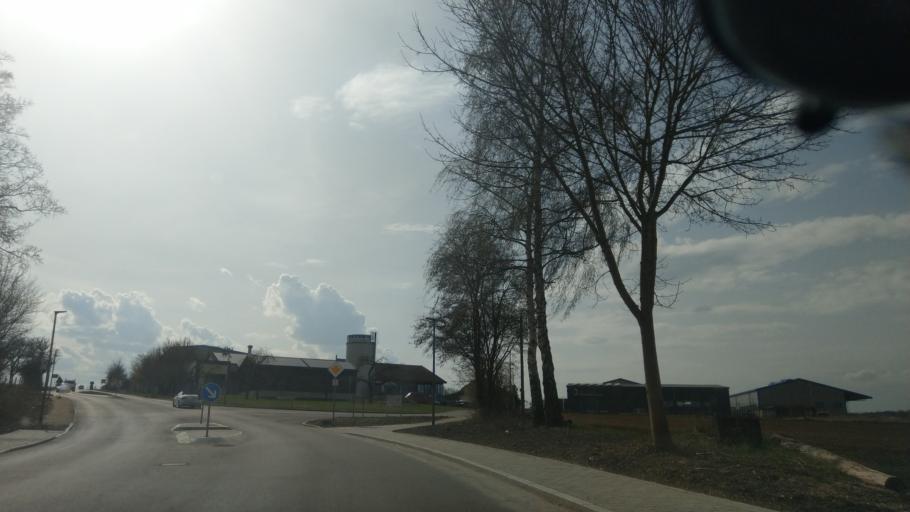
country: DE
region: Baden-Wuerttemberg
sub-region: Tuebingen Region
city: Asselfingen
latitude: 48.5295
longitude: 10.1875
